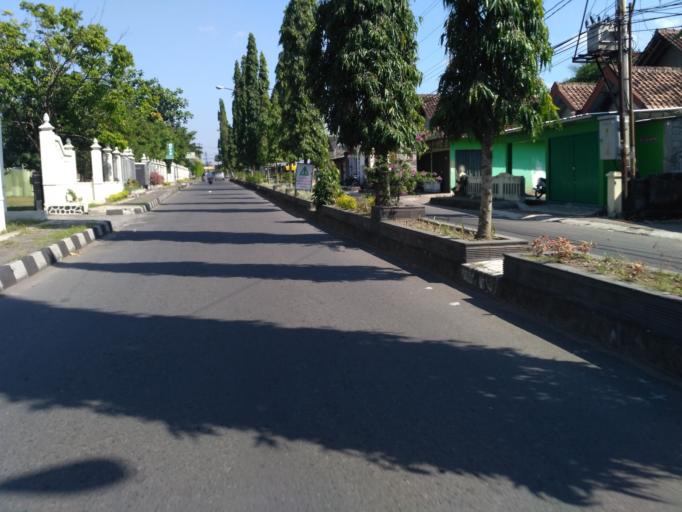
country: ID
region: Daerah Istimewa Yogyakarta
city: Depok
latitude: -7.7511
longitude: 110.4266
